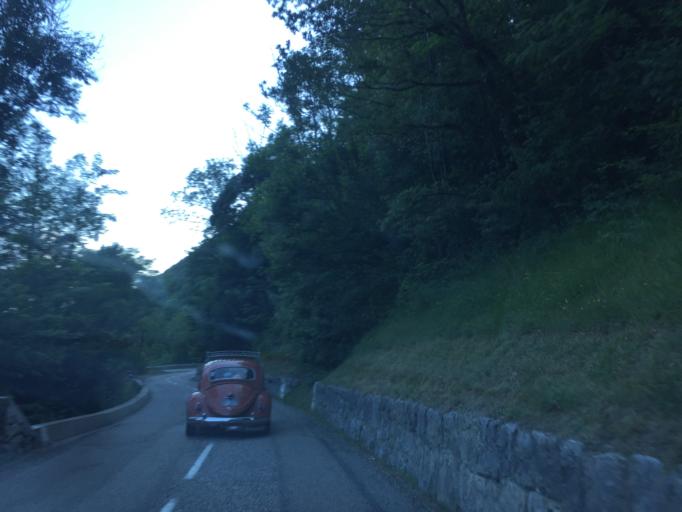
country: FR
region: Rhone-Alpes
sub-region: Departement de la Savoie
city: Challes-les-Eaux
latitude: 45.5486
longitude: 6.0075
